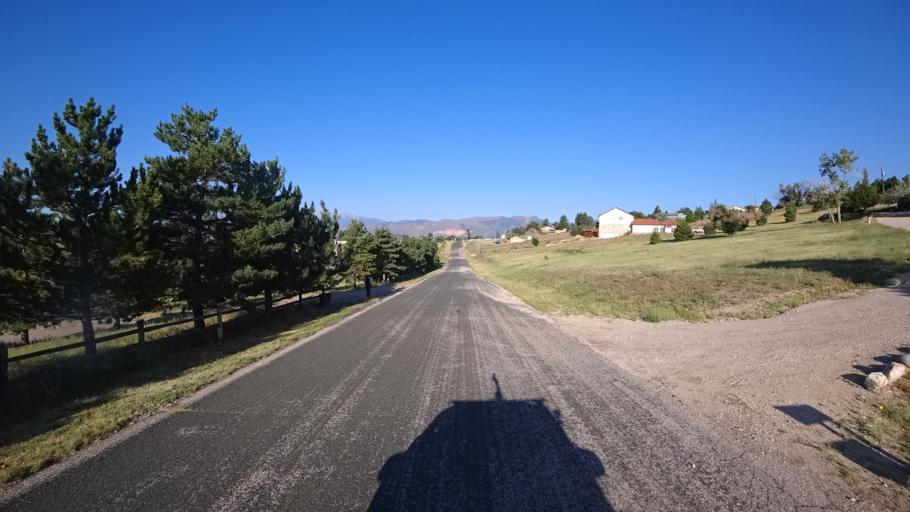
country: US
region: Colorado
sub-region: El Paso County
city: Black Forest
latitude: 38.9367
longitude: -104.7693
